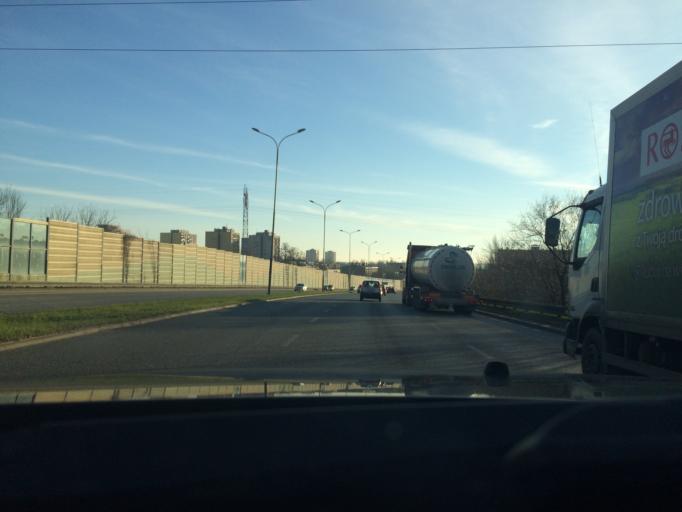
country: PL
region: Lodz Voivodeship
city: Lodz
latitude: 51.7414
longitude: 19.4418
